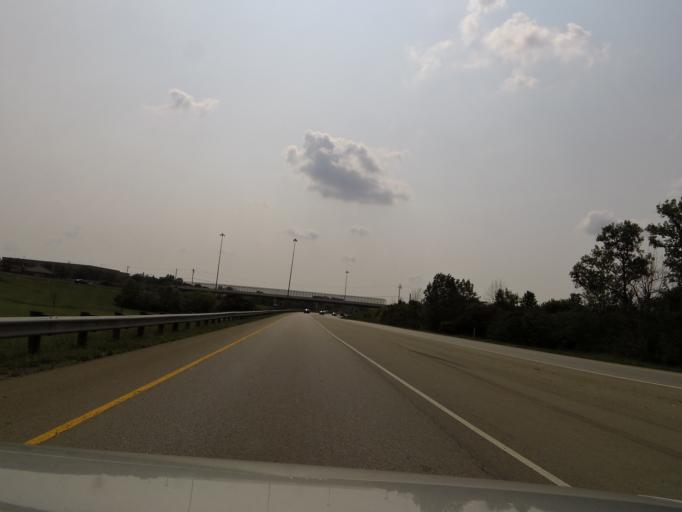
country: US
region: Ohio
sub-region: Hamilton County
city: Glendale
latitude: 39.2919
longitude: -84.4441
